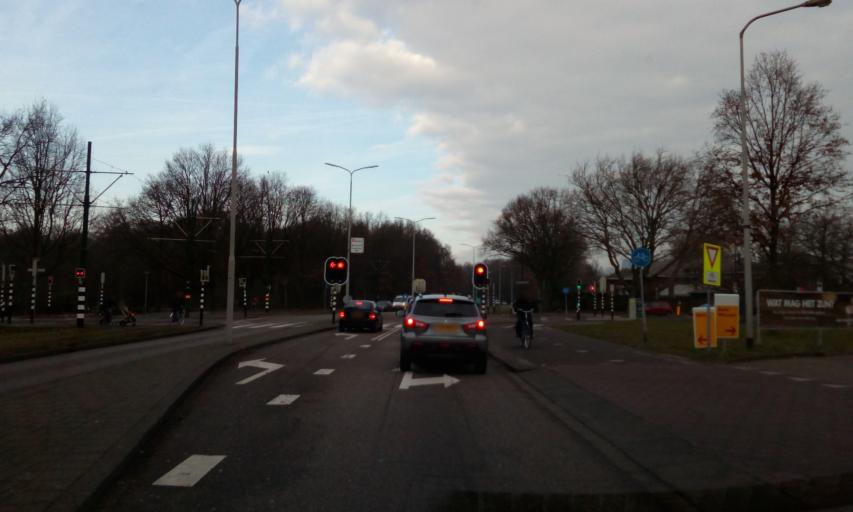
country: NL
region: South Holland
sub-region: Gemeente Rijswijk
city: Rijswijk
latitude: 52.0518
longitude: 4.3281
